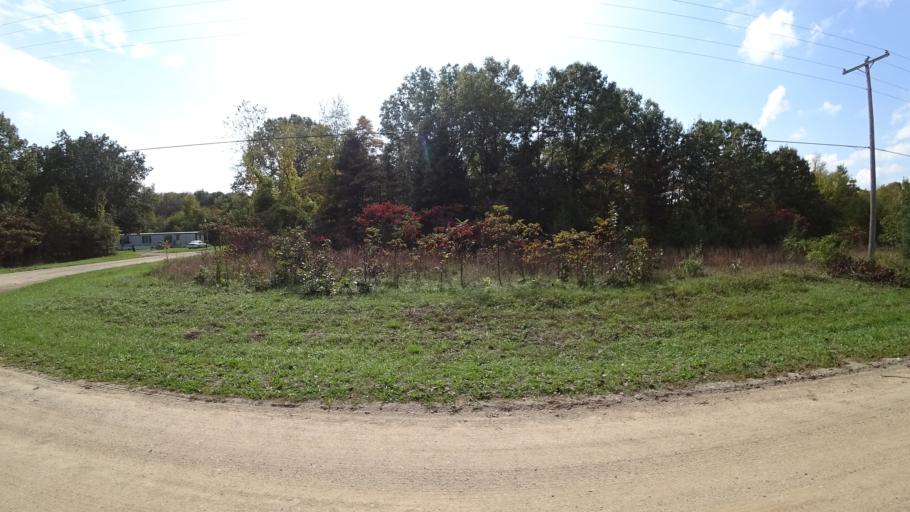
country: US
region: Michigan
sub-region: Saint Joseph County
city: Three Rivers
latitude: 41.9364
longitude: -85.6032
